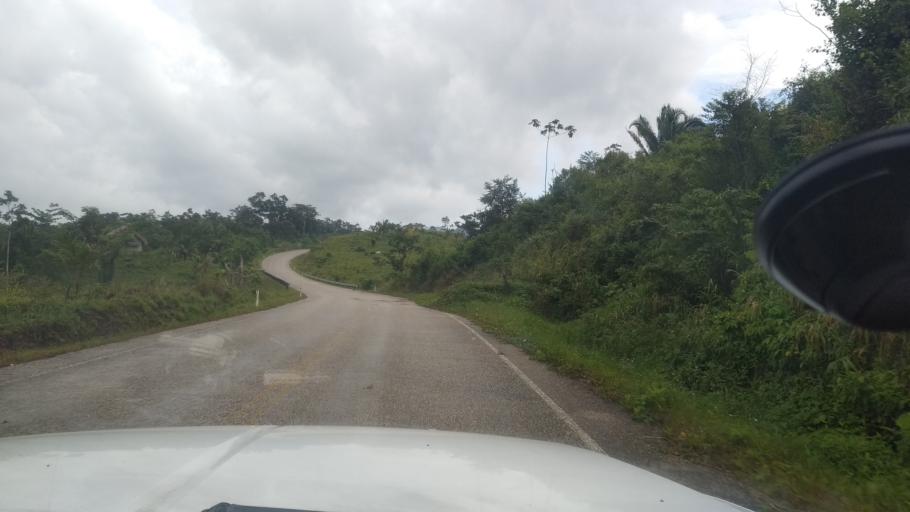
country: GT
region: Peten
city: San Luis
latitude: 16.1988
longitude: -89.1551
